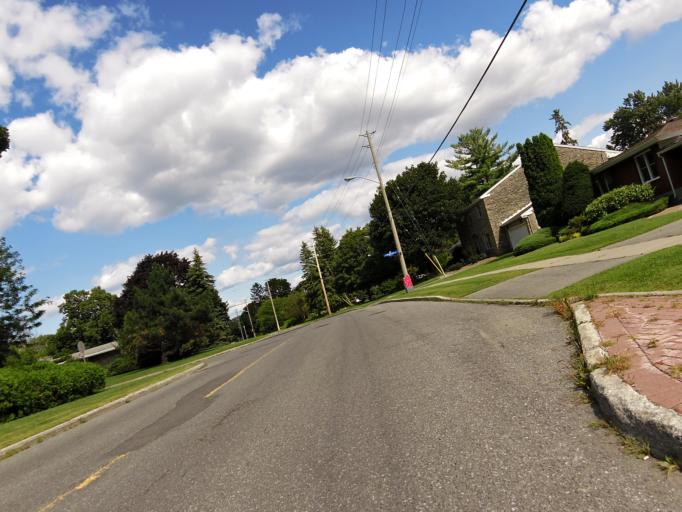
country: CA
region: Ontario
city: Ottawa
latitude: 45.3706
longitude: -75.7607
